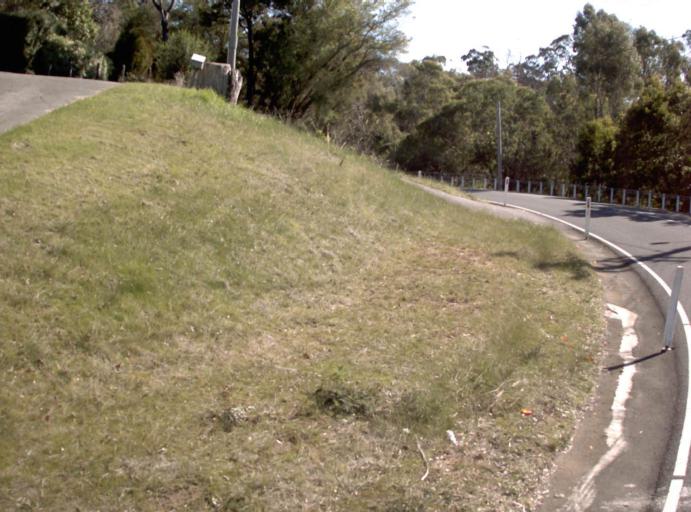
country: AU
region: Tasmania
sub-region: Launceston
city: East Launceston
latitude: -41.4565
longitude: 147.1653
